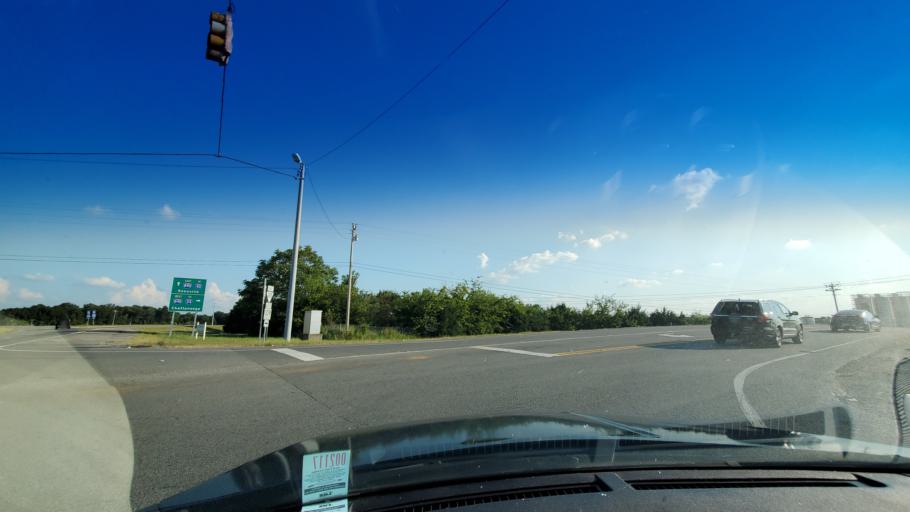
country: US
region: Tennessee
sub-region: Wilson County
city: Rural Hill
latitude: 36.1319
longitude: -86.4013
